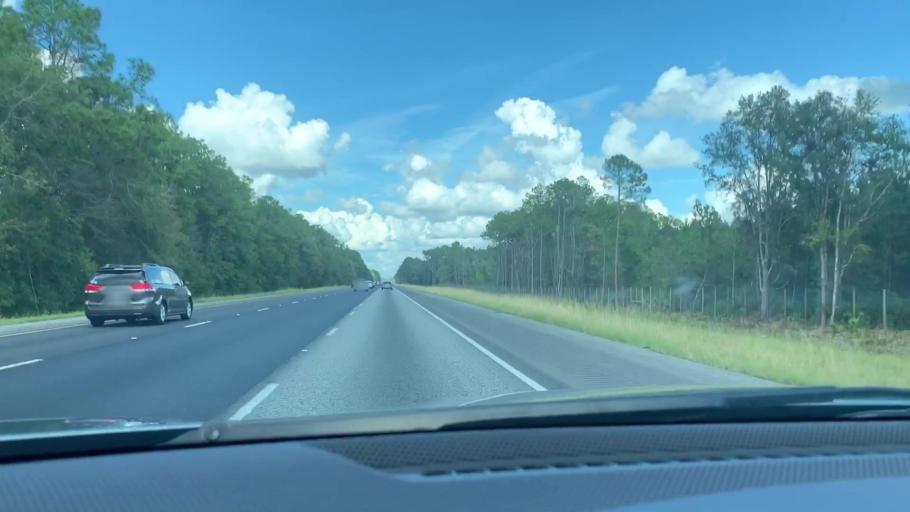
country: US
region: Georgia
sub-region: Camden County
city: Woodbine
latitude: 30.9022
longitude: -81.6857
